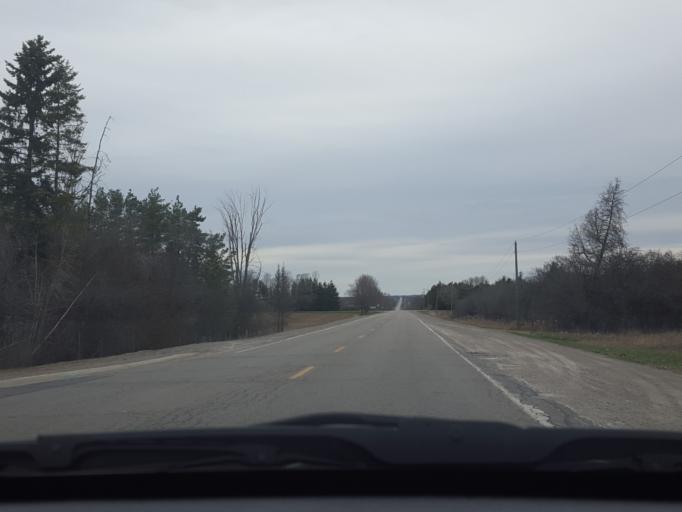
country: CA
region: Ontario
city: Uxbridge
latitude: 44.2754
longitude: -79.1614
